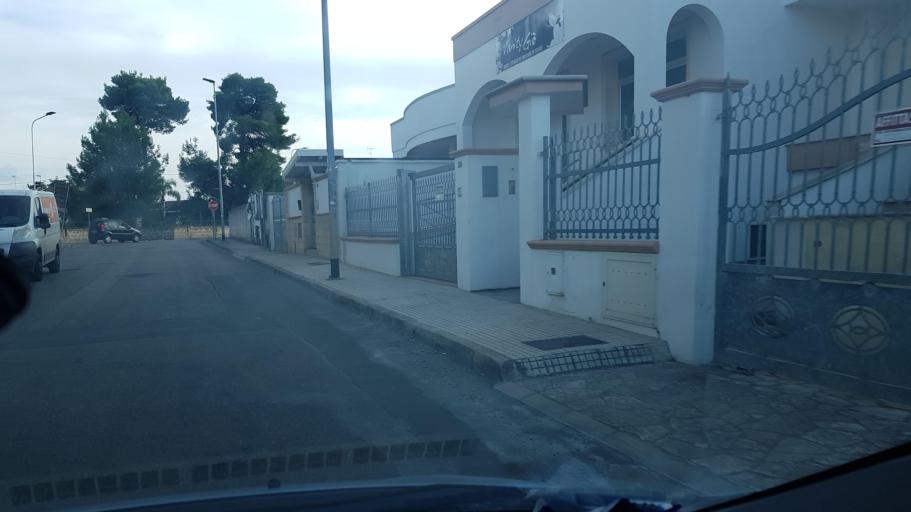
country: IT
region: Apulia
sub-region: Provincia di Lecce
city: Carmiano
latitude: 40.3415
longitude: 18.0397
